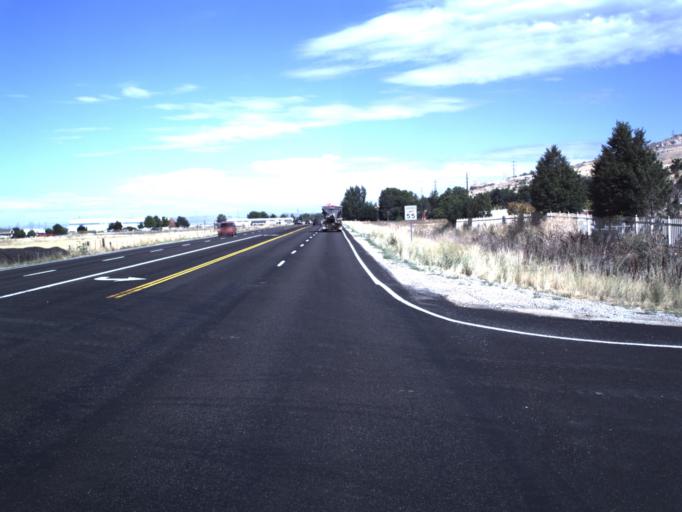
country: US
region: Utah
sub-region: Weber County
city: Pleasant View
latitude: 41.3212
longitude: -112.0166
